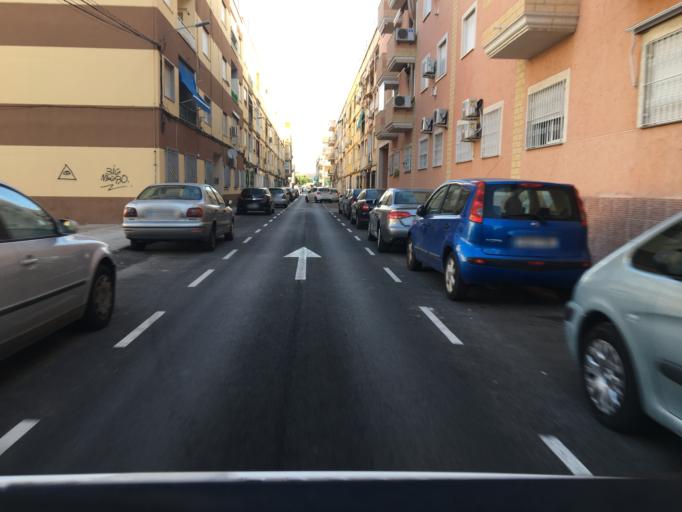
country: ES
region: Murcia
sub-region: Murcia
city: Cartagena
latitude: 37.6198
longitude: -1.0003
